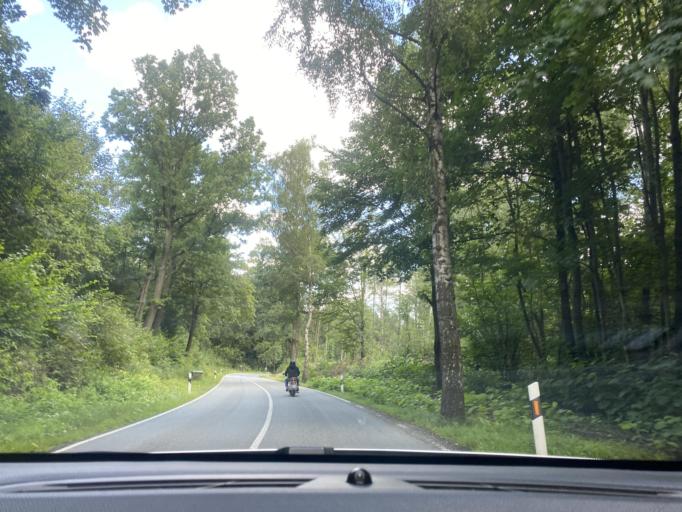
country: DE
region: Saxony
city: Schonbach
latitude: 51.0693
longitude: 14.5827
